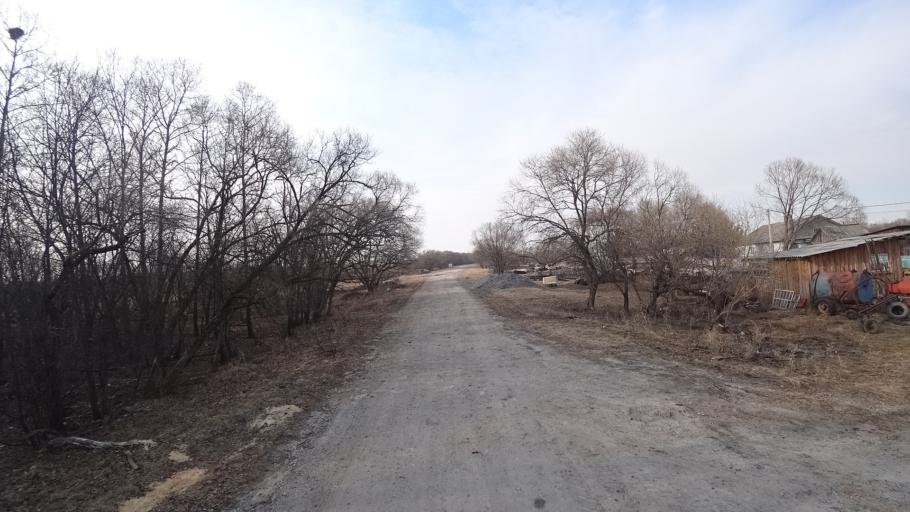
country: RU
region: Amur
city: Novobureyskiy
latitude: 49.8949
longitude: 129.8747
